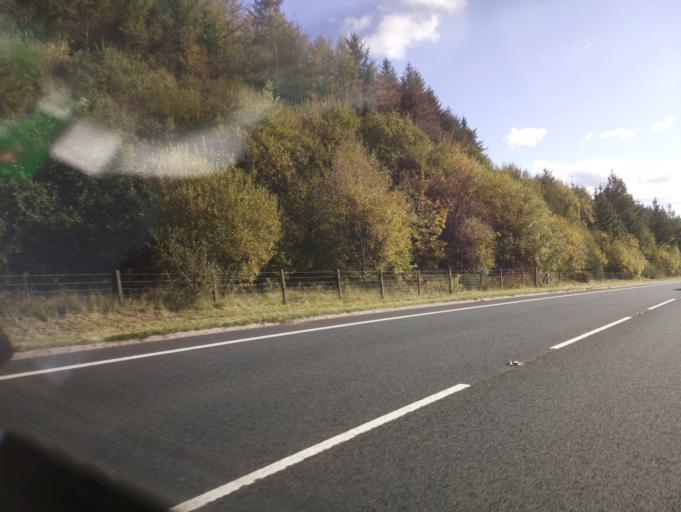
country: GB
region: Wales
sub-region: Rhondda Cynon Taf
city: Hirwaun
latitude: 51.8433
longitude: -3.4641
